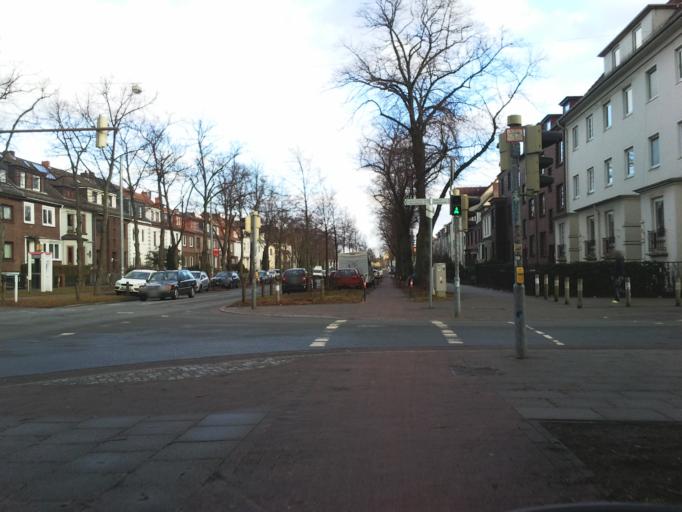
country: DE
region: Bremen
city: Bremen
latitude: 53.1009
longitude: 8.7814
